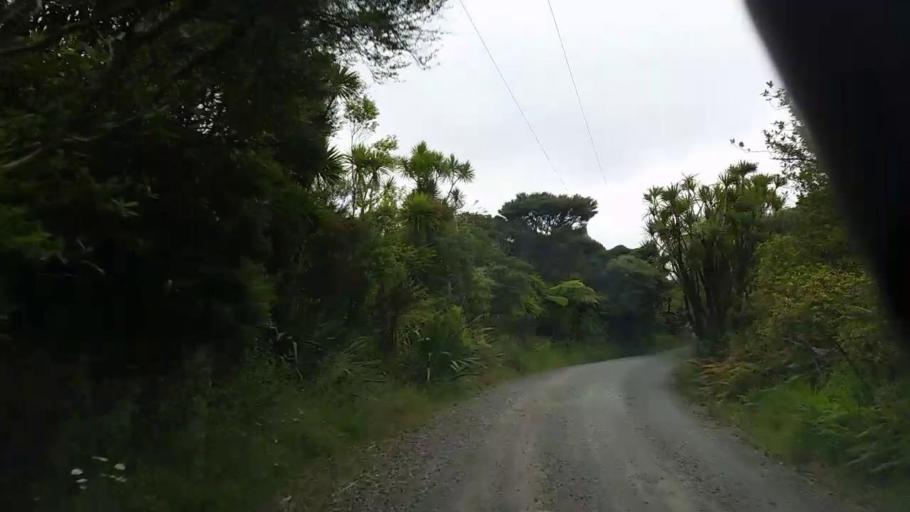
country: NZ
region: Auckland
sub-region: Auckland
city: Muriwai Beach
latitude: -36.9307
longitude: 174.5041
